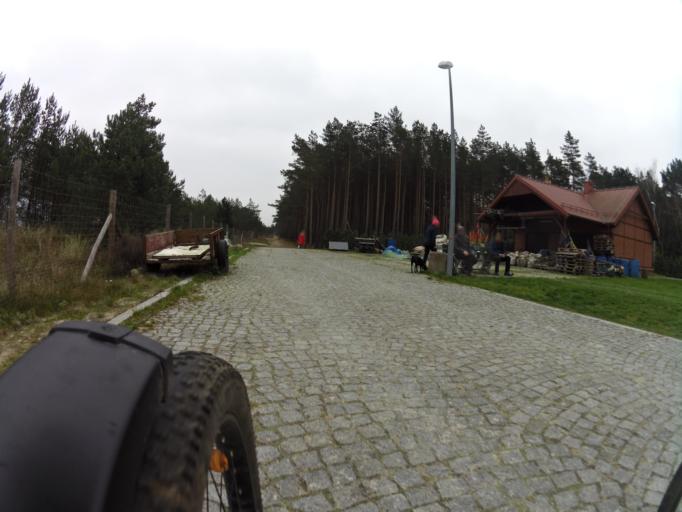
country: PL
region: Pomeranian Voivodeship
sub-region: Powiat pucki
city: Krokowa
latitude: 54.8324
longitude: 18.0890
